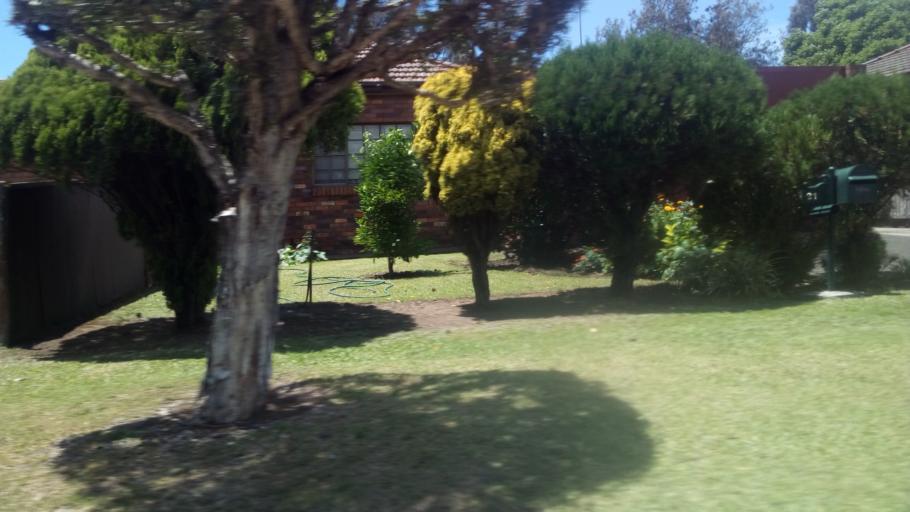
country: AU
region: New South Wales
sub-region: Wollongong
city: Mangerton
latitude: -34.4366
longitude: 150.8671
